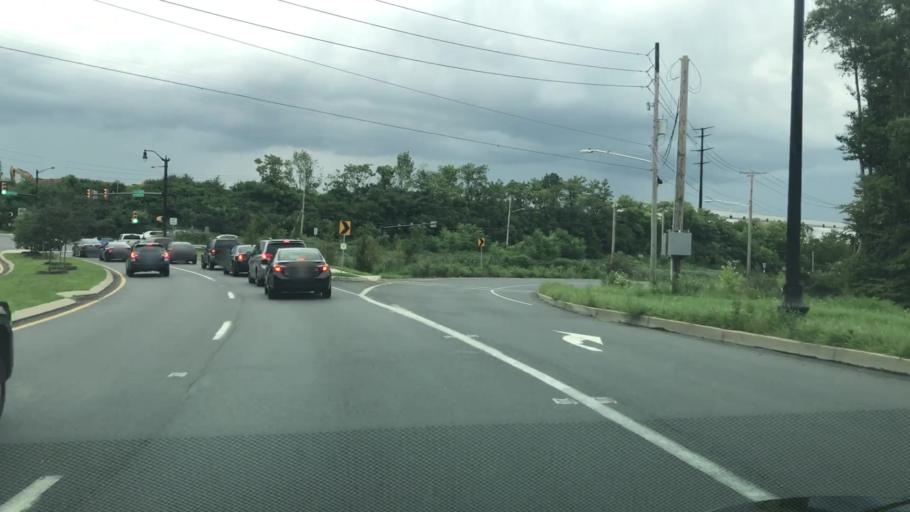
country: US
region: Pennsylvania
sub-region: Northampton County
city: Freemansburg
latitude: 40.6090
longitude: -75.3394
